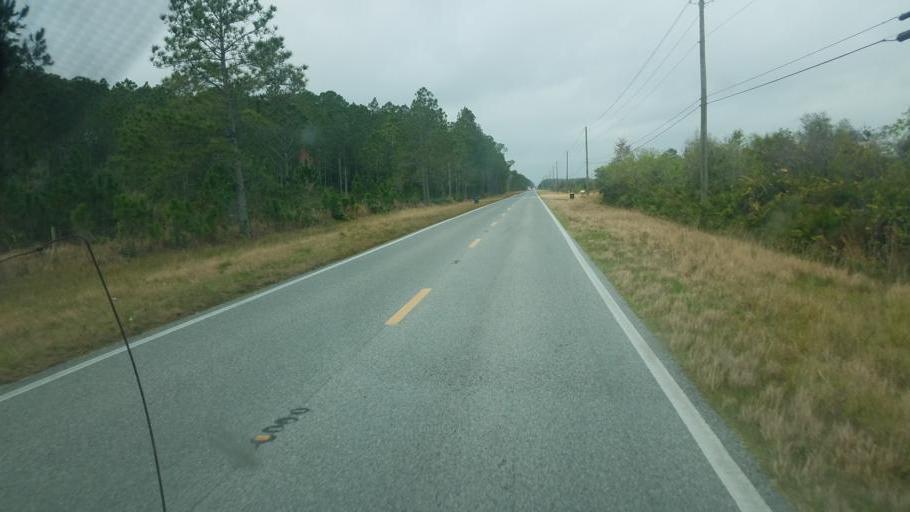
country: US
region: Florida
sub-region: Polk County
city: Polk City
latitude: 28.2591
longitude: -81.8835
